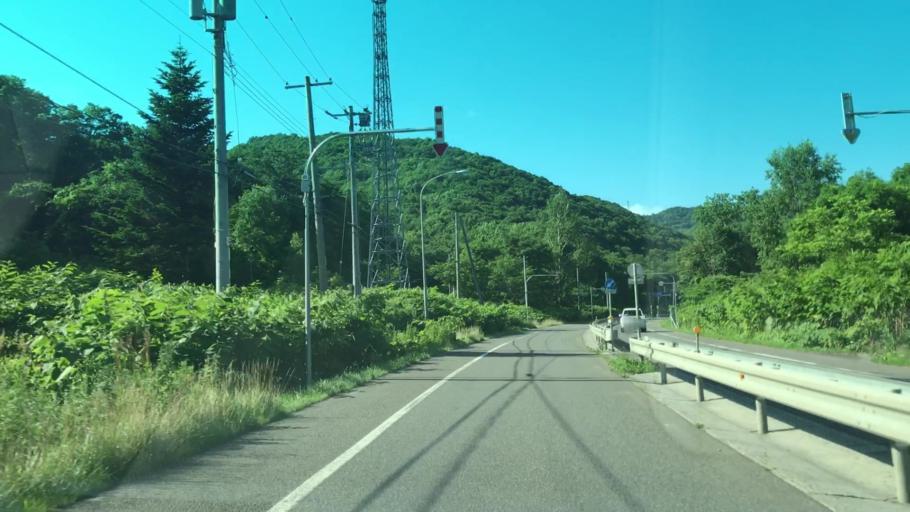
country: JP
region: Hokkaido
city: Iwanai
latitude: 43.0080
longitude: 140.6656
